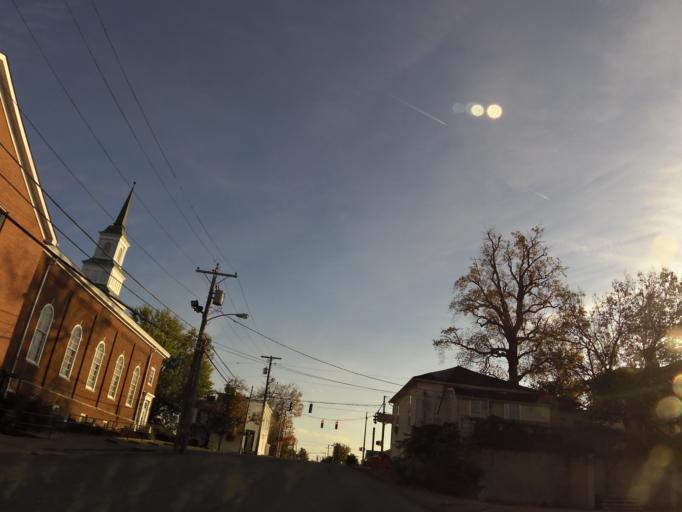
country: US
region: Kentucky
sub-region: Garrard County
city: Lancaster
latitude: 37.6198
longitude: -84.5770
